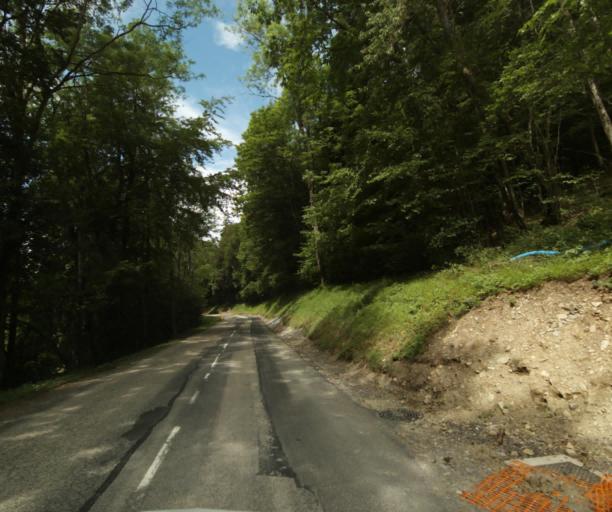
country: FR
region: Rhone-Alpes
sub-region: Departement de la Haute-Savoie
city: Perrignier
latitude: 46.2949
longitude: 6.4648
